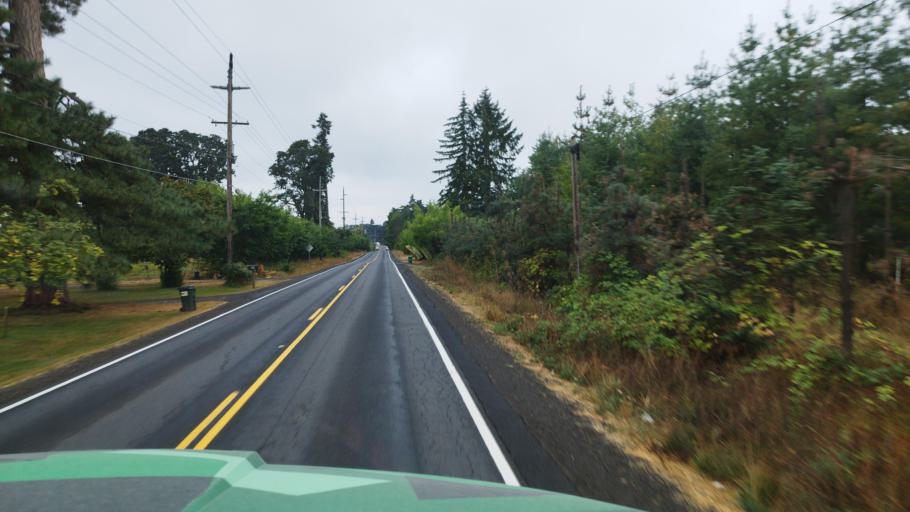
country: US
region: Oregon
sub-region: Washington County
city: Cornelius
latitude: 45.5314
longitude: -123.0811
